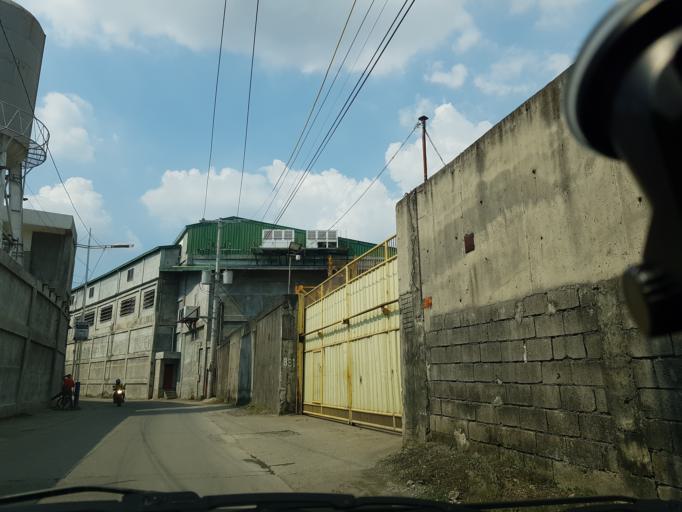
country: PH
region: Calabarzon
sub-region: Province of Rizal
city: Pateros
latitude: 14.5440
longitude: 121.0852
